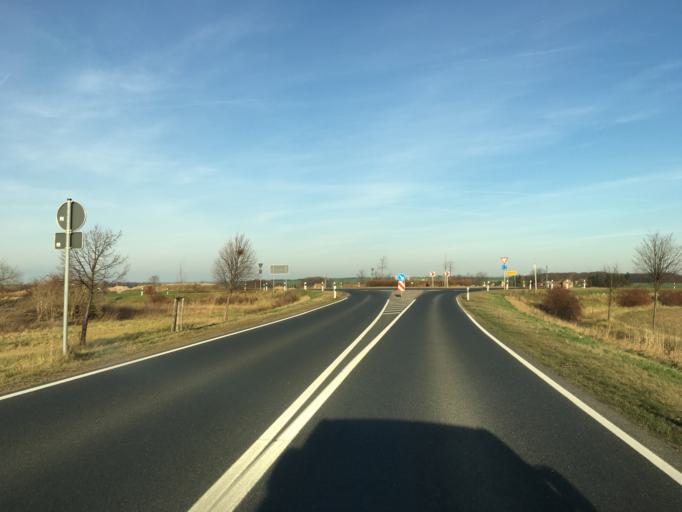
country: DE
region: Saxony
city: Naundorf
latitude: 51.2512
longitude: 13.1630
